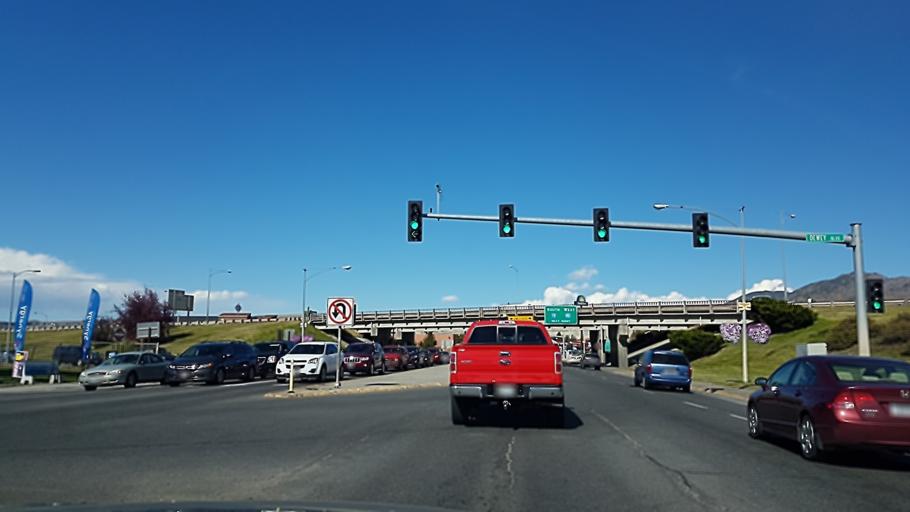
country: US
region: Montana
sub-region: Silver Bow County
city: Butte
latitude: 45.9833
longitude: -112.5082
